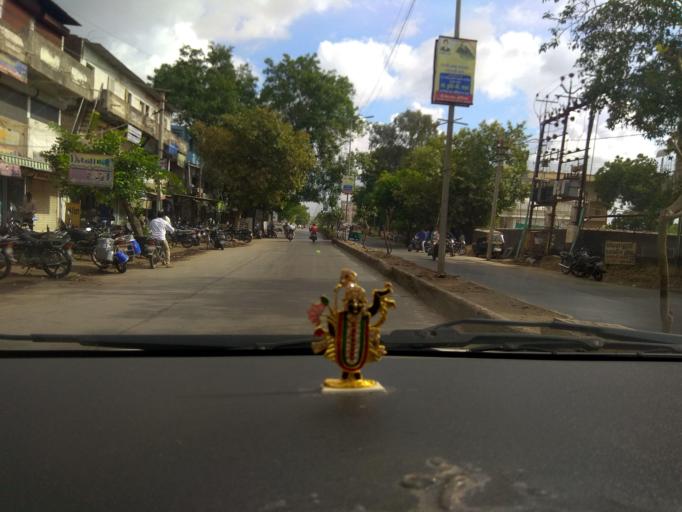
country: IN
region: Gujarat
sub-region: Bhavnagar
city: Bhavnagar
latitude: 21.7458
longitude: 72.1487
